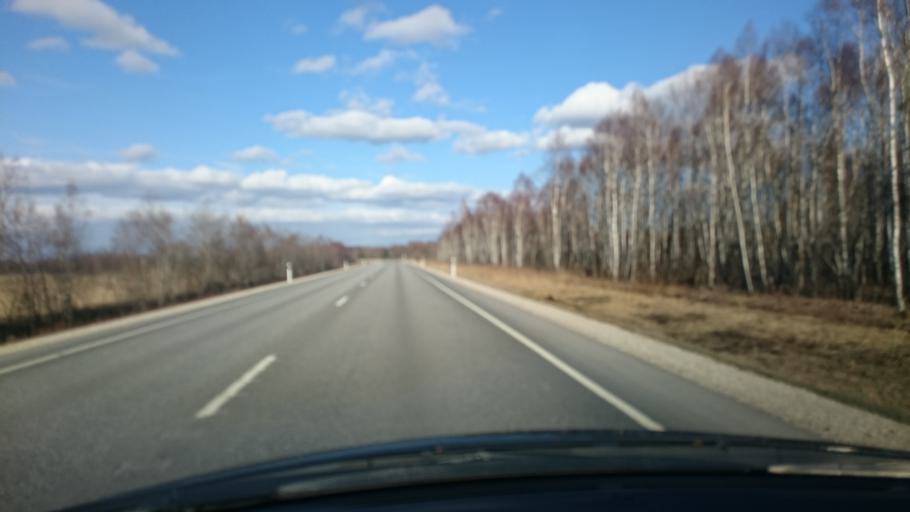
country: EE
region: Laeaene
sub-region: Lihula vald
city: Lihula
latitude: 58.7907
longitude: 24.0320
